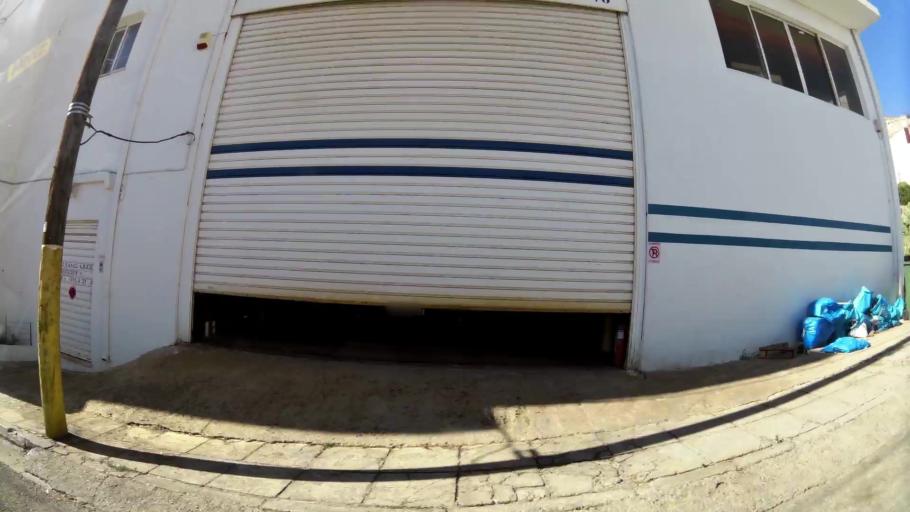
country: GR
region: Attica
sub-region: Nomos Piraios
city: Keratsini
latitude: 37.9654
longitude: 23.6070
